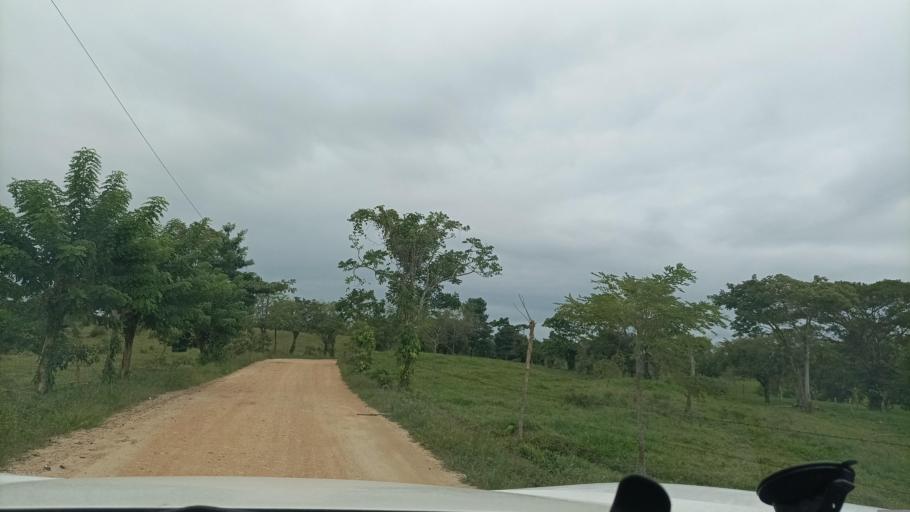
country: MX
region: Veracruz
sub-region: Uxpanapa
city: Poblado Cinco
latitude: 17.4778
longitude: -94.5699
